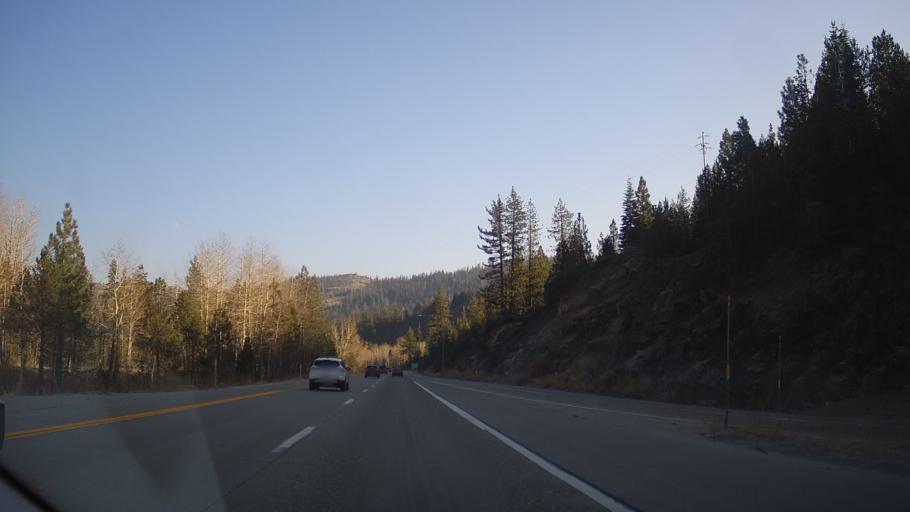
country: US
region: California
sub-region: Nevada County
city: Truckee
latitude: 39.3088
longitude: -120.5427
